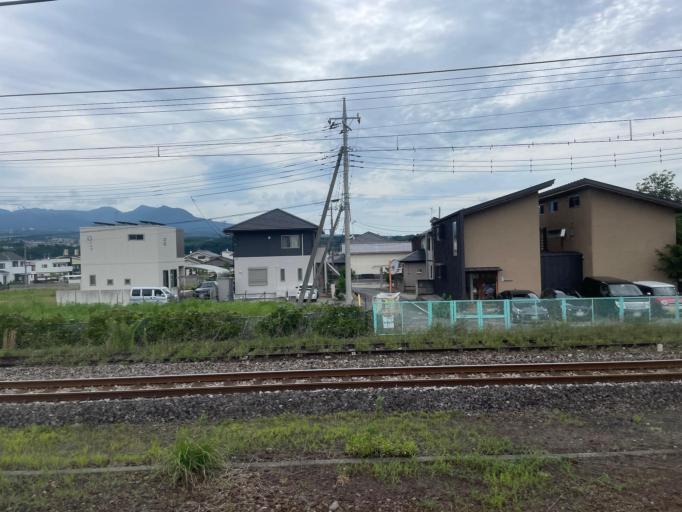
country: JP
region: Gunma
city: Shibukawa
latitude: 36.4629
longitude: 139.0195
